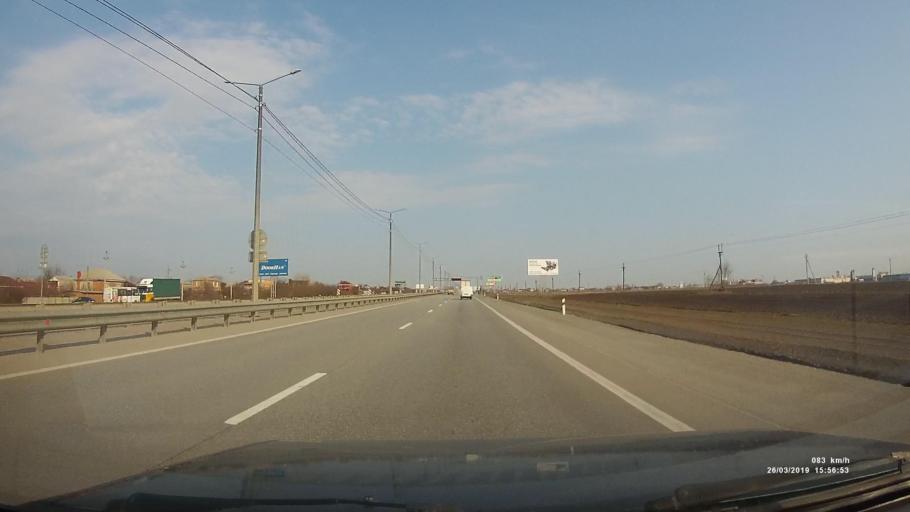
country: RU
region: Rostov
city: Kalinin
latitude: 47.2640
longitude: 39.6011
